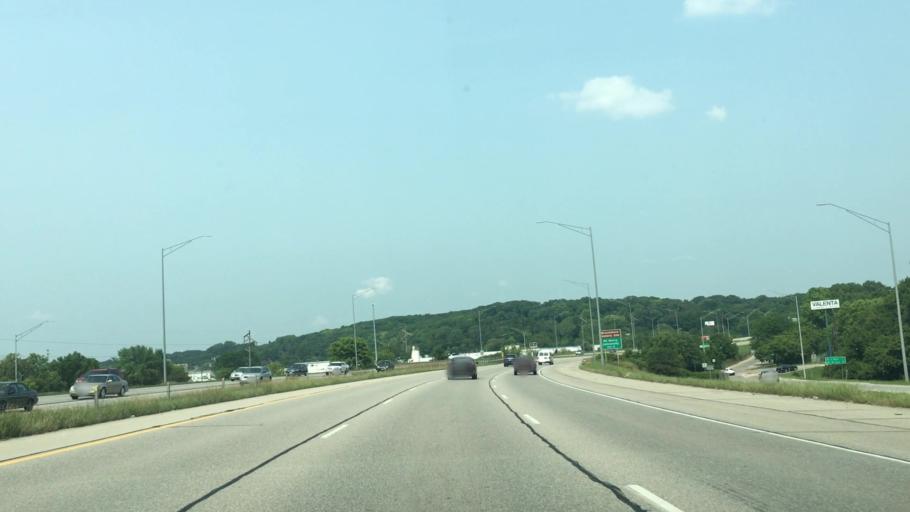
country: US
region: Iowa
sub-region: Linn County
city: Cedar Rapids
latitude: 41.9940
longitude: -91.6655
